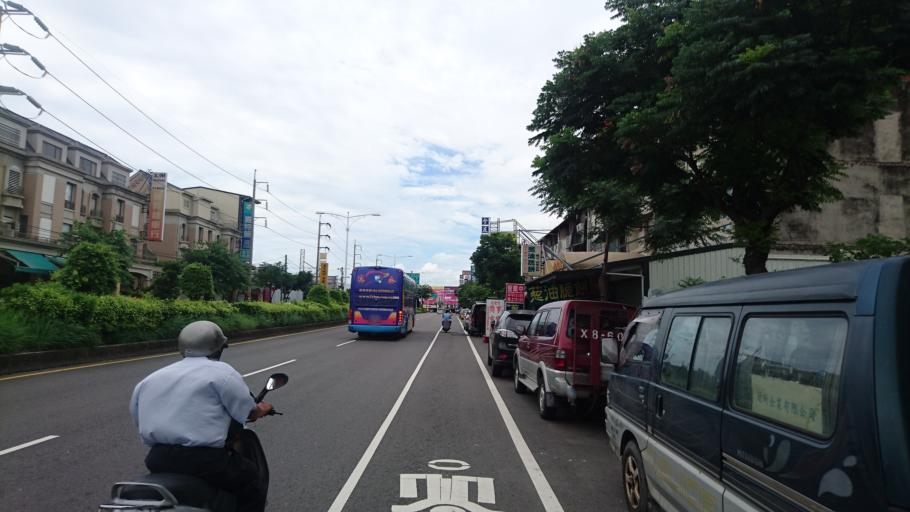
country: TW
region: Taiwan
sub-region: Taichung City
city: Taichung
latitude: 24.0674
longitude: 120.6963
